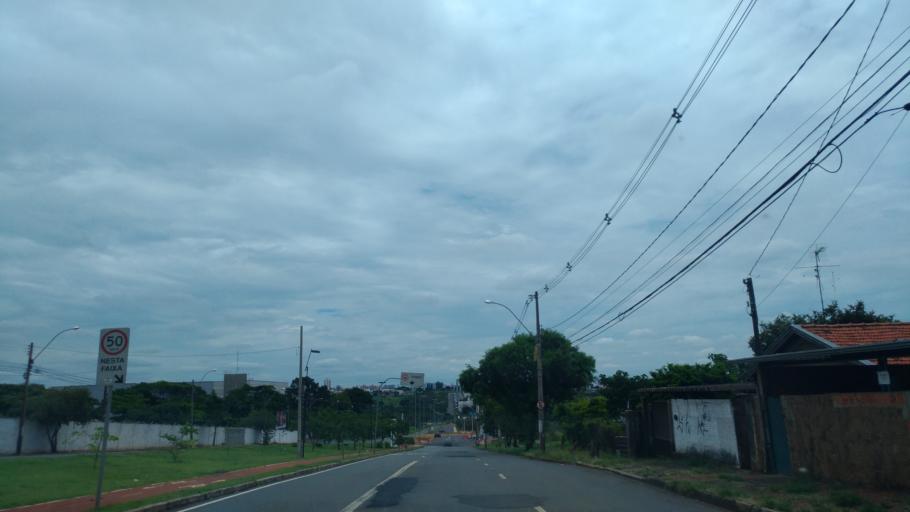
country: BR
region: Sao Paulo
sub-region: Nova Odessa
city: Nova Odessa
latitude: -22.7699
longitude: -47.3143
